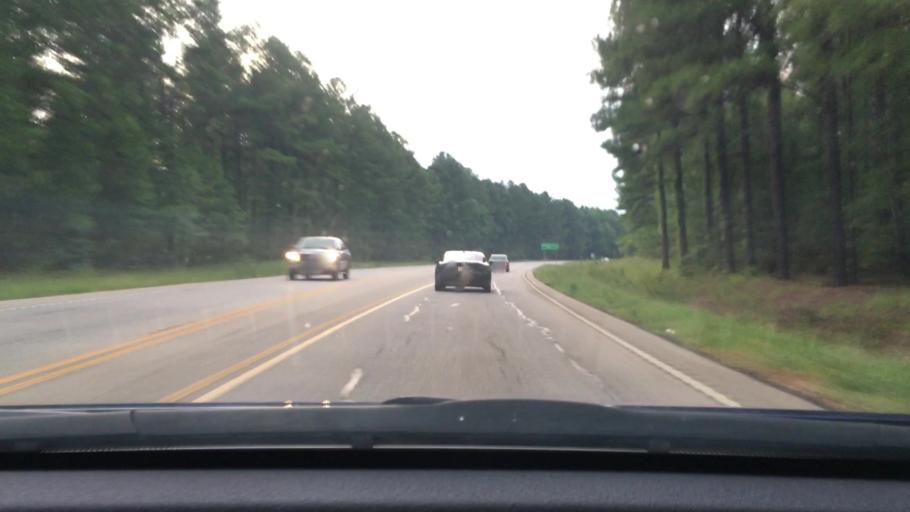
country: US
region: South Carolina
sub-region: Sumter County
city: Cherryvale
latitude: 33.9435
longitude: -80.4917
